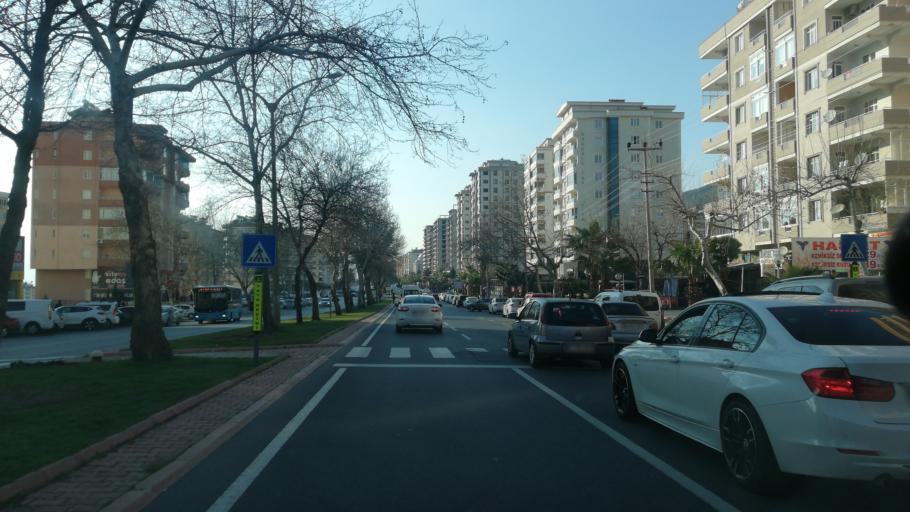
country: TR
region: Kahramanmaras
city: Kahramanmaras
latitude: 37.5911
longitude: 36.8702
